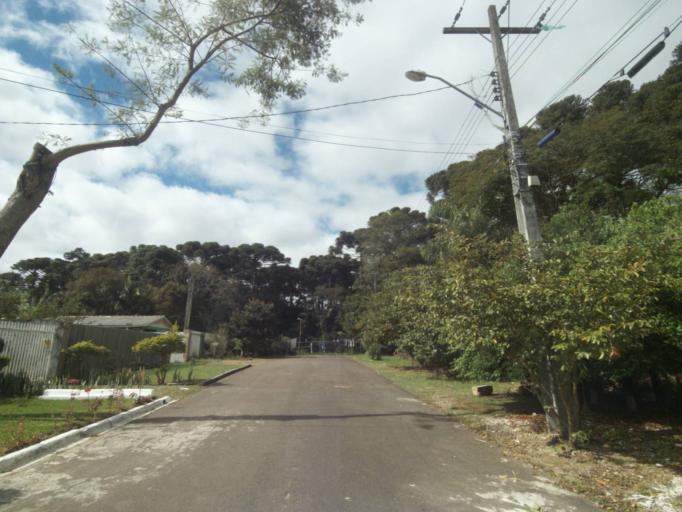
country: BR
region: Parana
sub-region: Sao Jose Dos Pinhais
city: Sao Jose dos Pinhais
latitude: -25.5358
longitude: -49.2888
